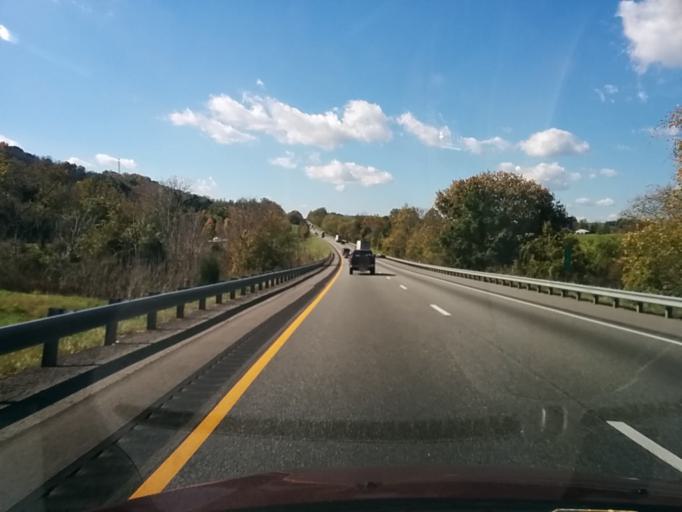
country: US
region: Virginia
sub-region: Botetourt County
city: Buchanan
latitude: 37.4915
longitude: -79.7663
